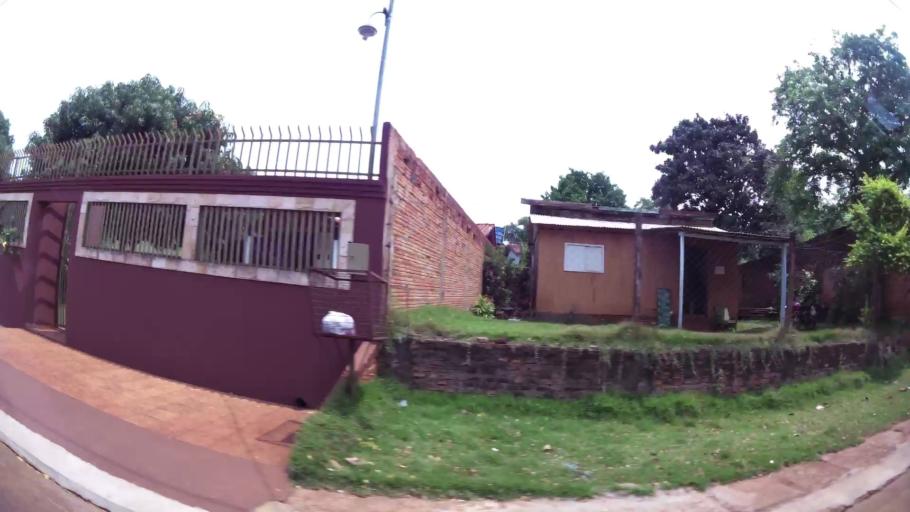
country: BR
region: Parana
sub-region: Foz Do Iguacu
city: Foz do Iguacu
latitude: -25.5697
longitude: -54.6064
